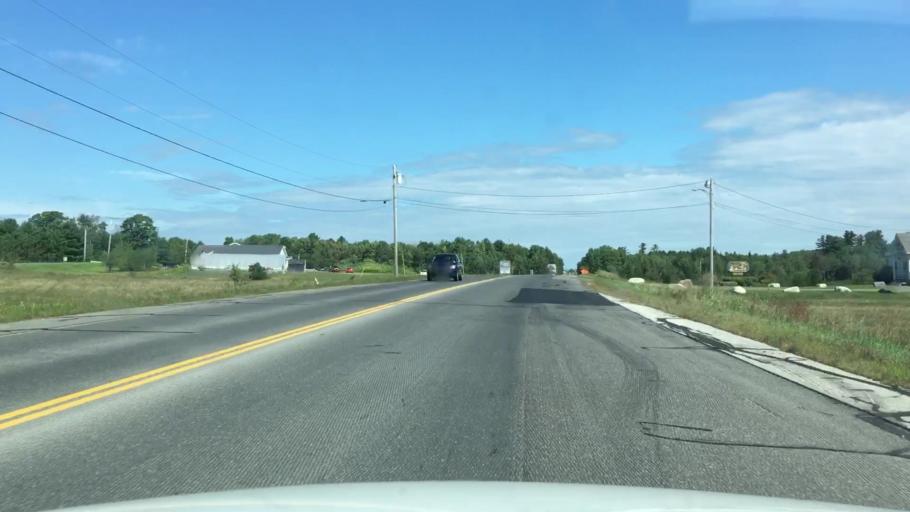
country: US
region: Maine
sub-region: Penobscot County
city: Newport
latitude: 44.8616
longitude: -69.2845
